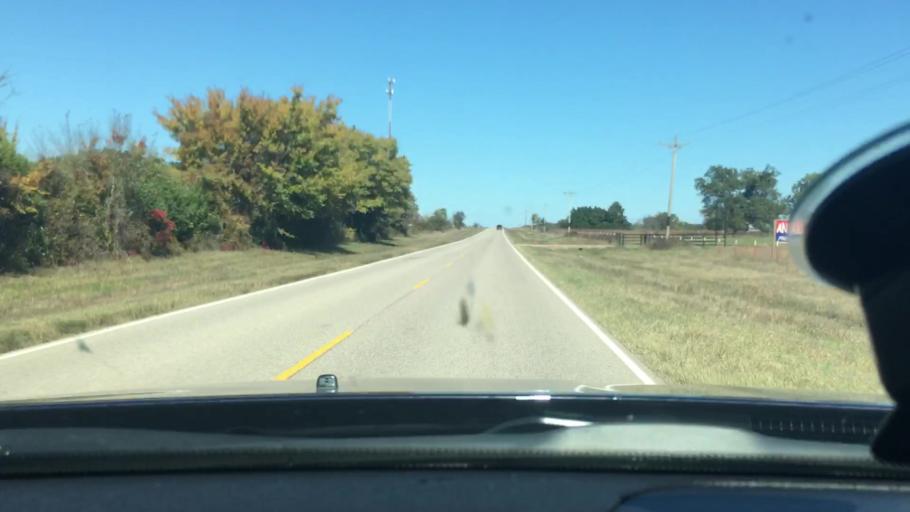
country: US
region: Oklahoma
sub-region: Johnston County
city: Tishomingo
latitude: 34.4274
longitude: -96.6361
